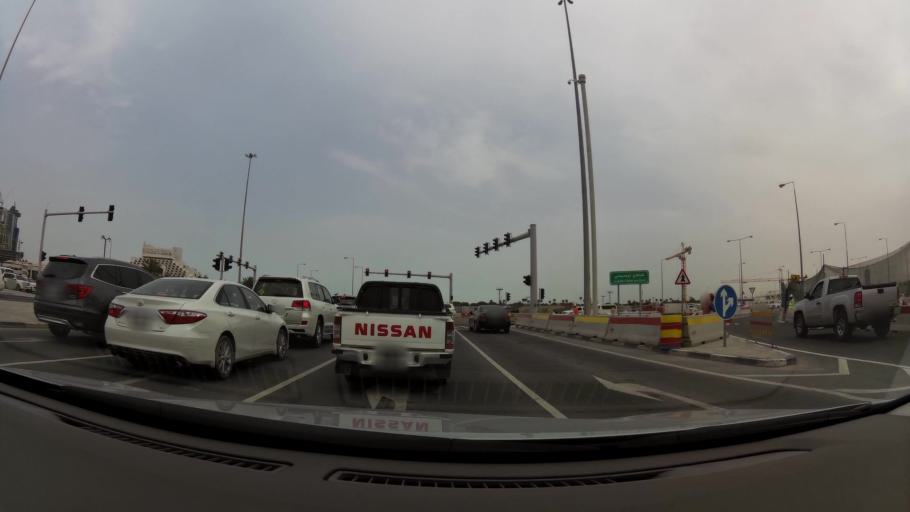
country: QA
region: Baladiyat ad Dawhah
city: Doha
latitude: 25.3098
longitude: 51.5143
